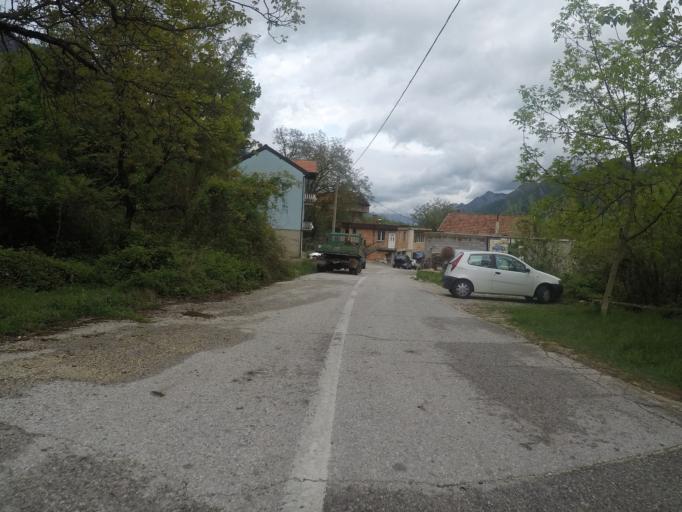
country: BA
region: Federation of Bosnia and Herzegovina
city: Kocerin
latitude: 43.5445
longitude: 17.5463
